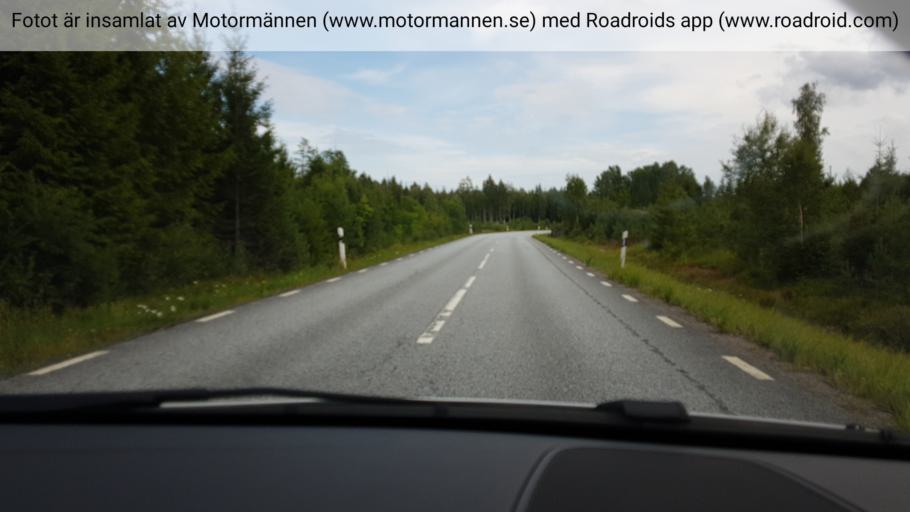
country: SE
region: Uppsala
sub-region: Osthammars Kommun
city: Anneberg
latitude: 60.1281
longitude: 18.4428
